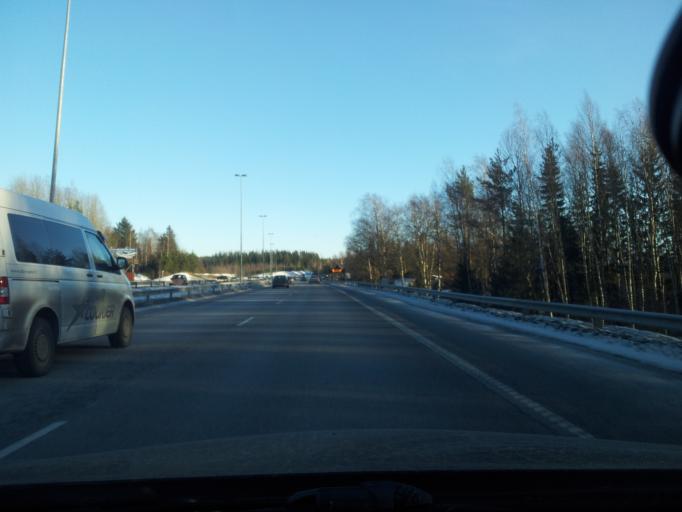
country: FI
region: Uusimaa
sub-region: Helsinki
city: Kirkkonummi
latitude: 60.2829
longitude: 24.4349
